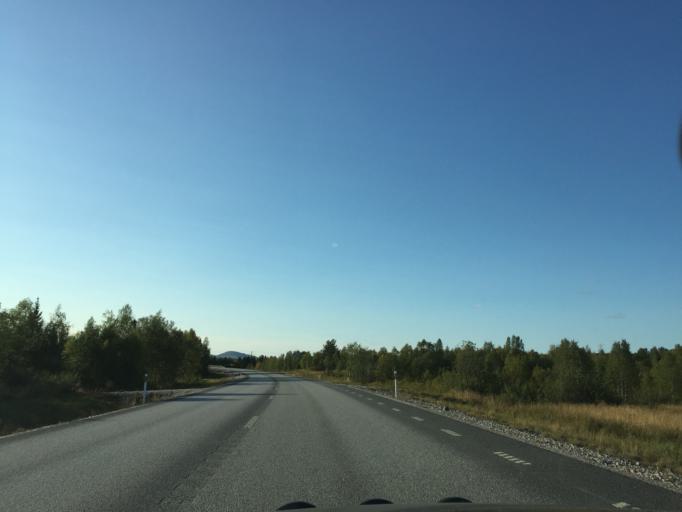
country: SE
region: Norrbotten
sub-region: Gallivare Kommun
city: Malmberget
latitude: 67.6422
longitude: 21.0567
